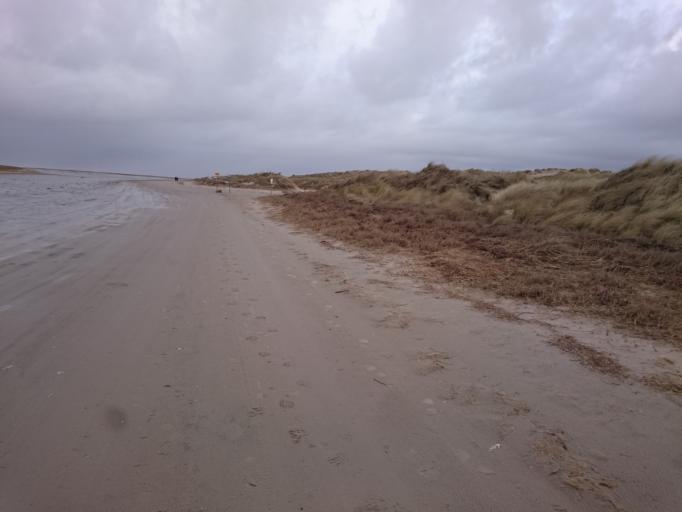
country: DK
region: South Denmark
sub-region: Fano Kommune
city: Nordby
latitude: 55.4268
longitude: 8.3688
